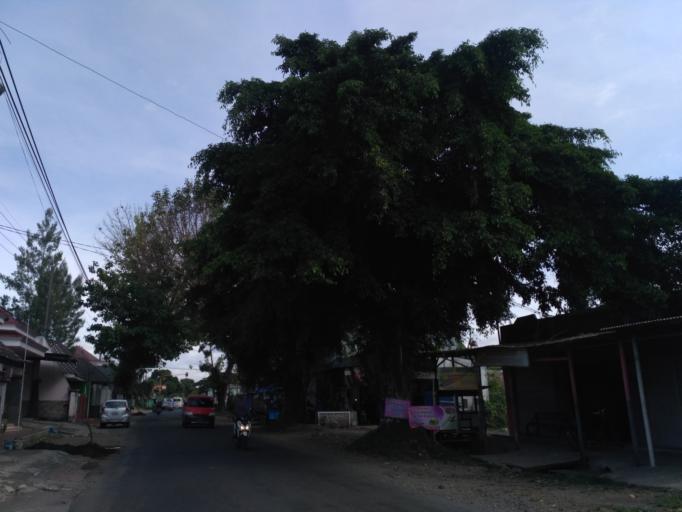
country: ID
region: East Java
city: Golek
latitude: -8.0625
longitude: 112.6268
